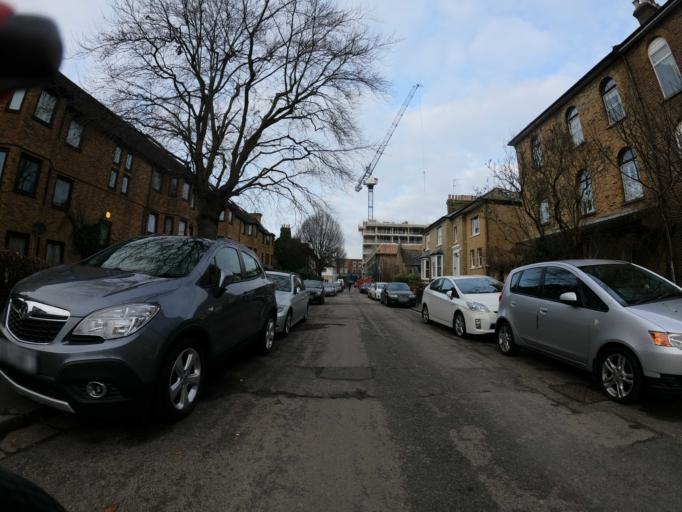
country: GB
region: England
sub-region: Greater London
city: Greenford
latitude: 51.5074
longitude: -0.3393
